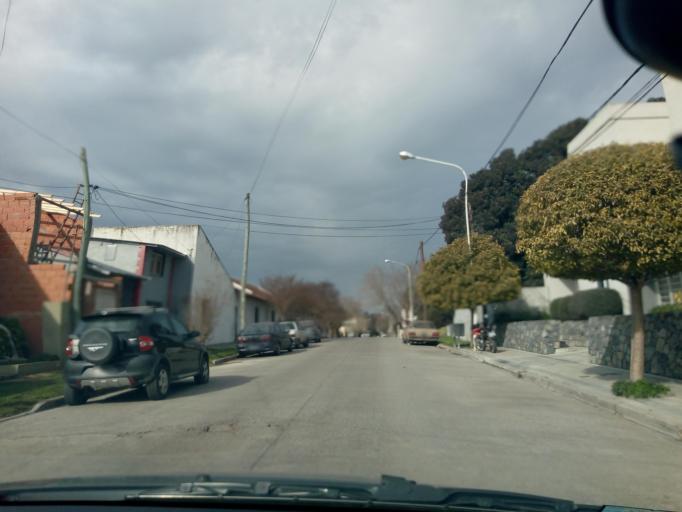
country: AR
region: Buenos Aires
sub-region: Partido de Tandil
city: Tandil
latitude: -37.3384
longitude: -59.1325
